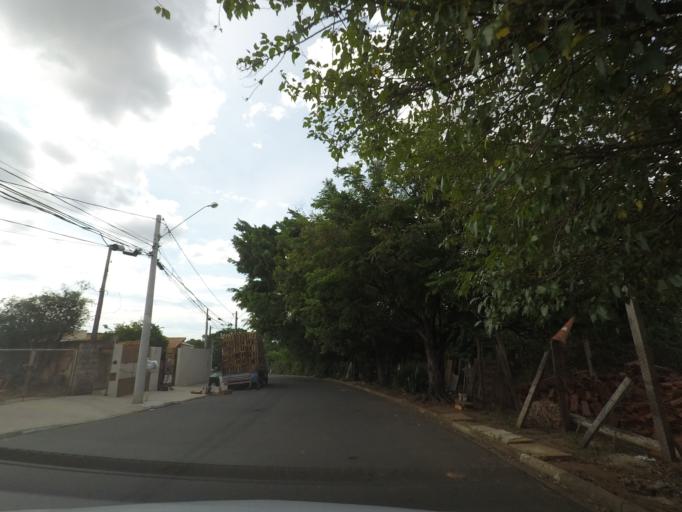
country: BR
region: Sao Paulo
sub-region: Campinas
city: Campinas
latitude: -22.8838
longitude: -47.1079
